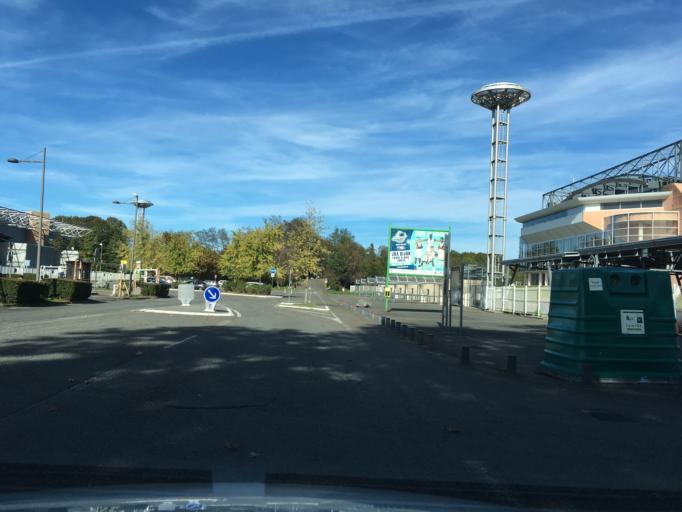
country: FR
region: Aquitaine
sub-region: Departement des Pyrenees-Atlantiques
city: Pau
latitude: 43.3337
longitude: -0.3643
